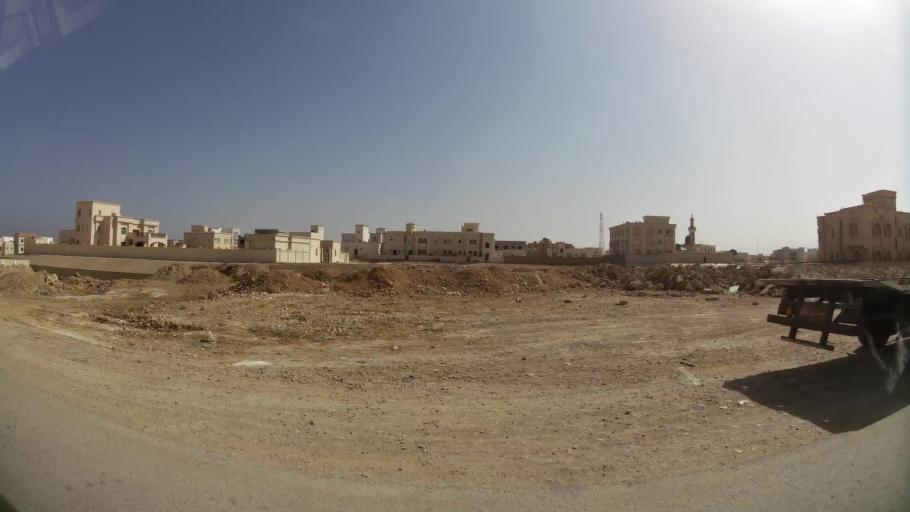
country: OM
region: Zufar
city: Salalah
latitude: 17.0018
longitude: 54.0163
